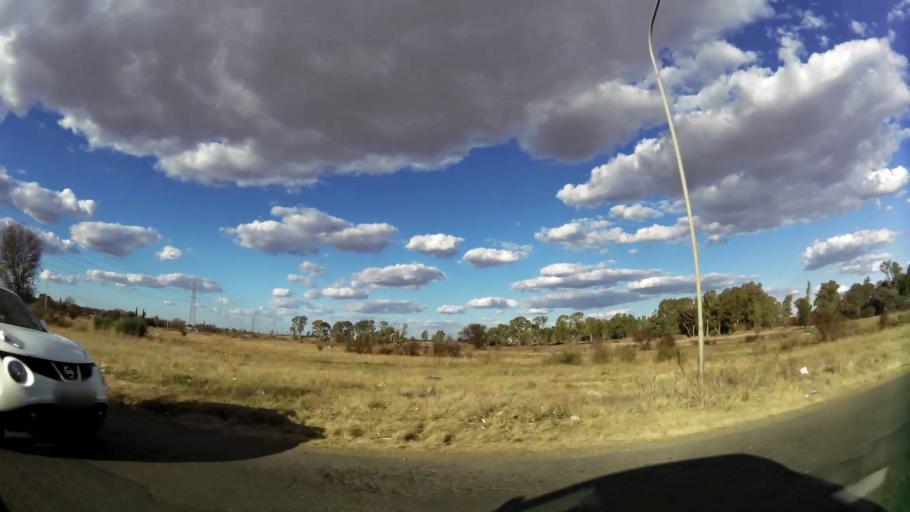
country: ZA
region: North-West
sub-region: Dr Kenneth Kaunda District Municipality
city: Potchefstroom
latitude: -26.7062
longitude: 27.0780
